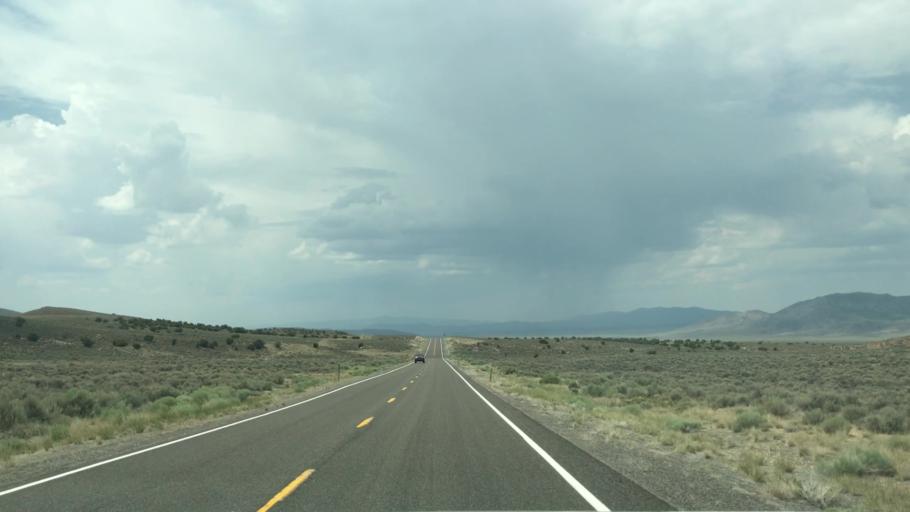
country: US
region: Nevada
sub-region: Eureka County
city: Eureka
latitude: 39.3978
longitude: -115.7134
